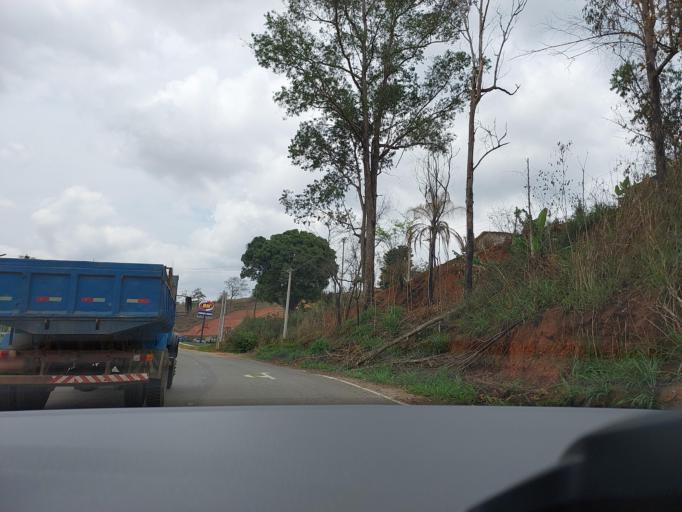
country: BR
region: Minas Gerais
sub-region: Ponte Nova
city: Ponte Nova
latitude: -20.4291
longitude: -42.8939
